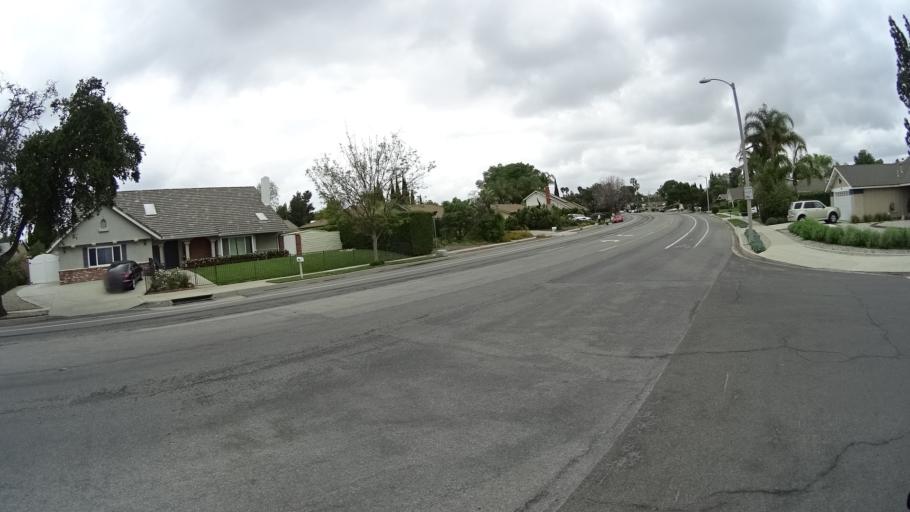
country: US
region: California
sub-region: Ventura County
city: Thousand Oaks
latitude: 34.2180
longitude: -118.8736
